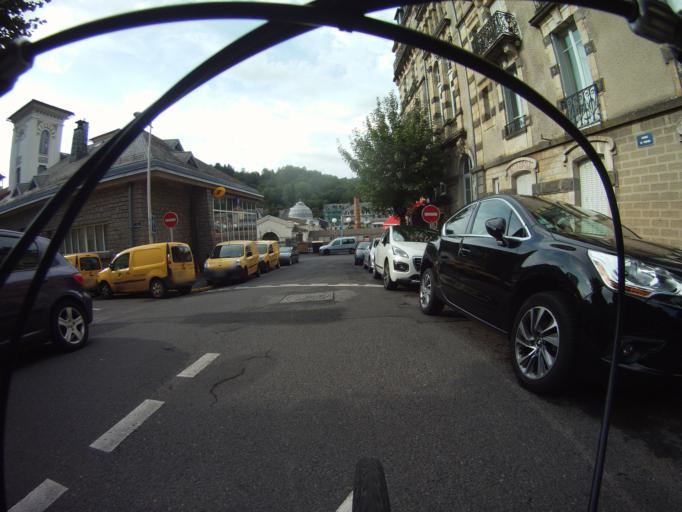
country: FR
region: Auvergne
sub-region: Departement du Puy-de-Dome
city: La Bourboule
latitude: 45.5875
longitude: 2.7394
